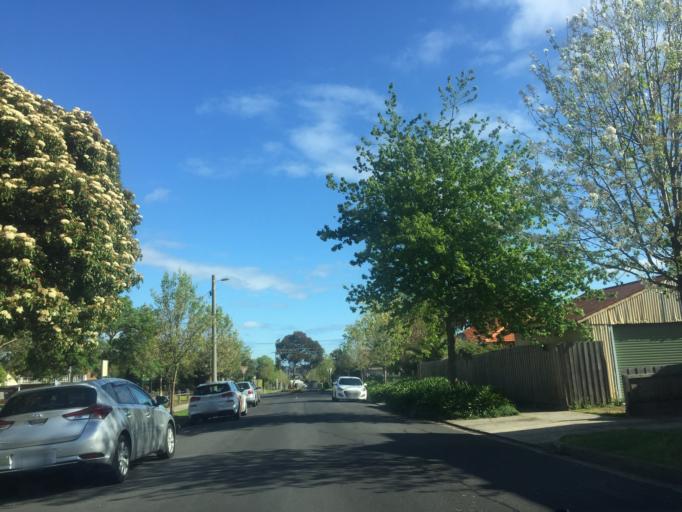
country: AU
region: Victoria
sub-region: Darebin
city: Reservoir
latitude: -37.7275
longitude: 145.0081
